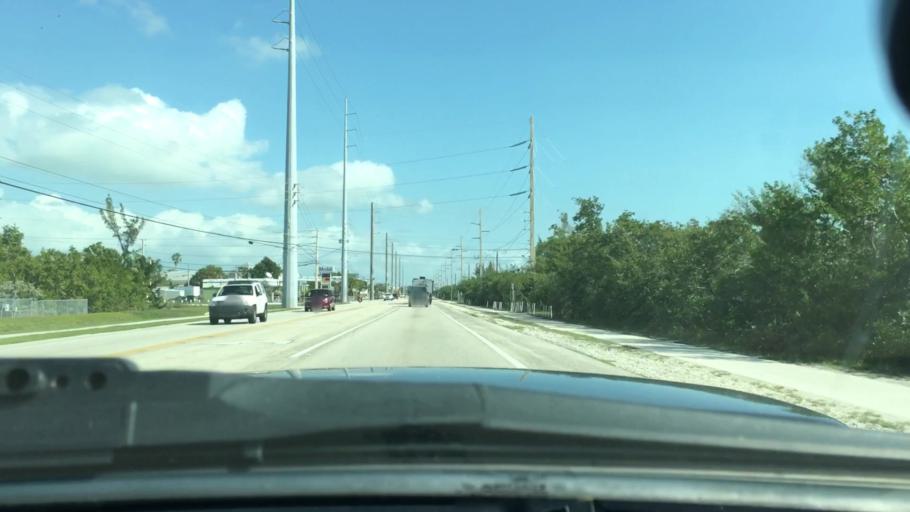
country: US
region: Florida
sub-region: Monroe County
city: Big Coppitt Key
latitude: 24.5954
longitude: -81.6603
